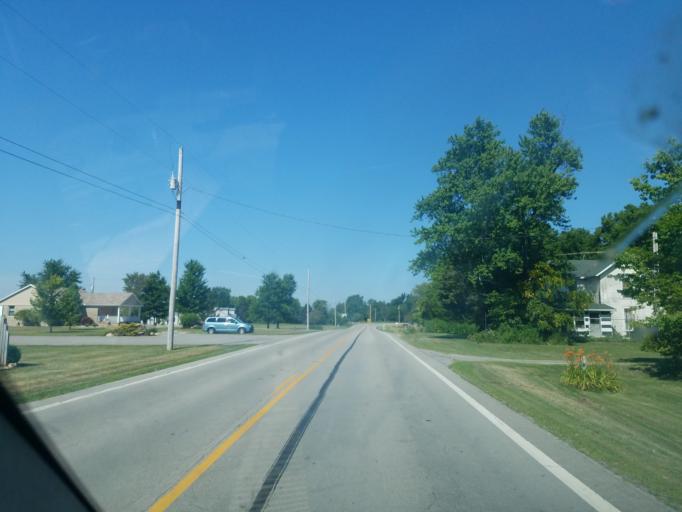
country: US
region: Ohio
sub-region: Logan County
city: Russells Point
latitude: 40.4639
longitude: -83.8257
